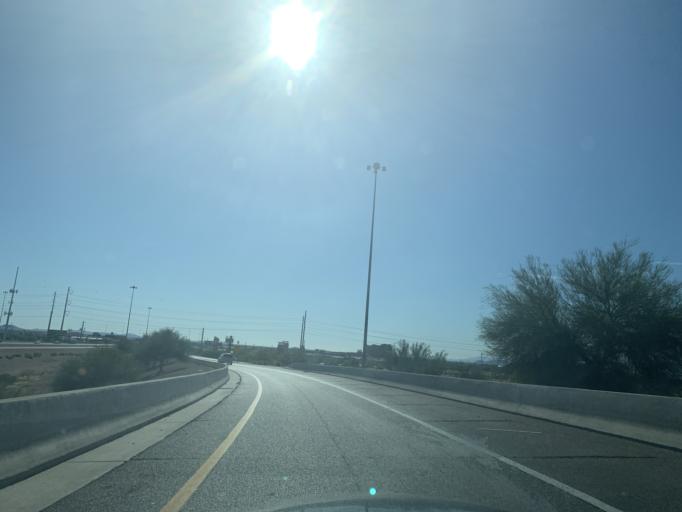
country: US
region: Arizona
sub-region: Maricopa County
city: Guadalupe
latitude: 33.2950
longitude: -111.9739
